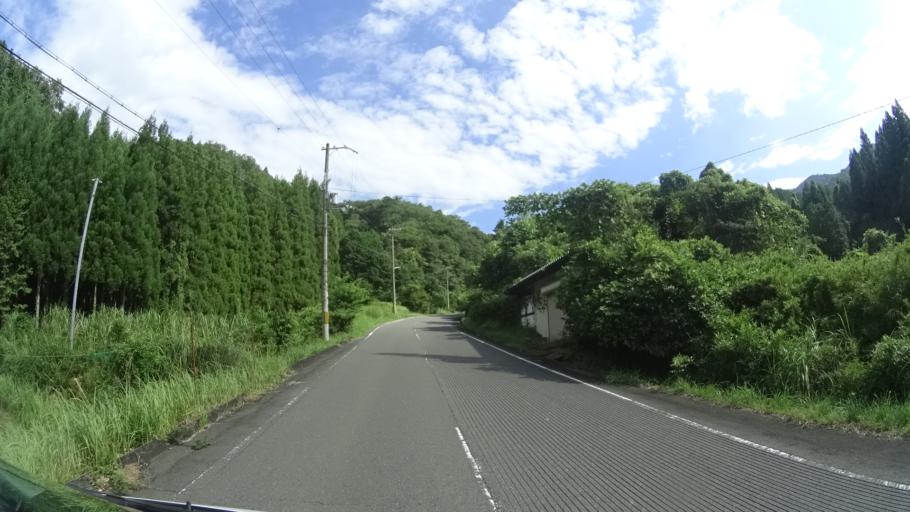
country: JP
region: Kyoto
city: Fukuchiyama
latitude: 35.3484
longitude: 135.1535
